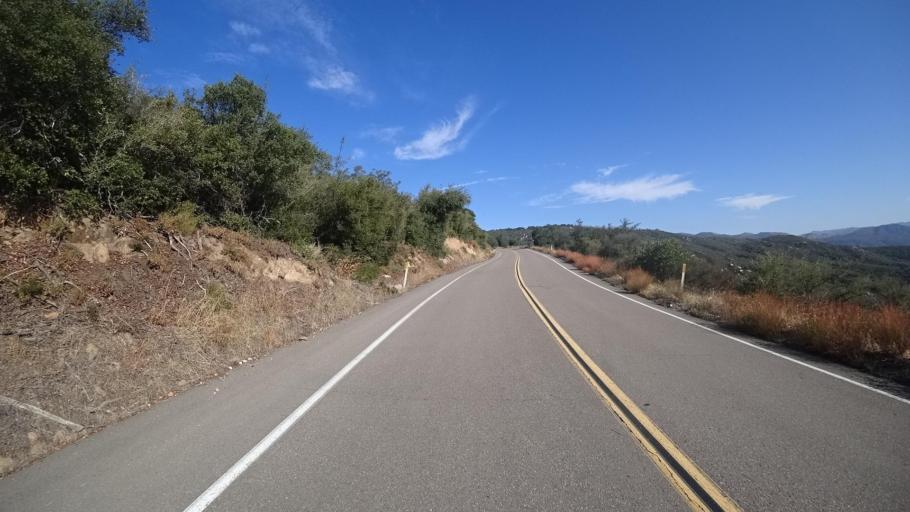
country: US
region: California
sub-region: Riverside County
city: Aguanga
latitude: 33.2630
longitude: -116.7661
